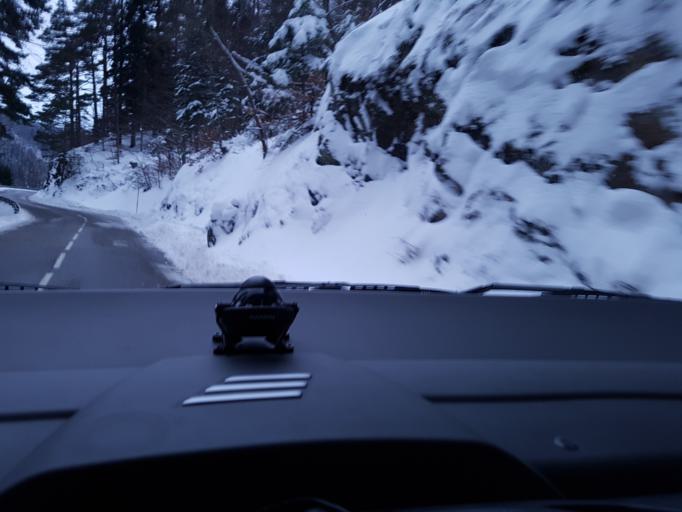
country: FR
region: Alsace
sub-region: Departement du Haut-Rhin
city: Lapoutroie
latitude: 48.2011
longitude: 7.1290
